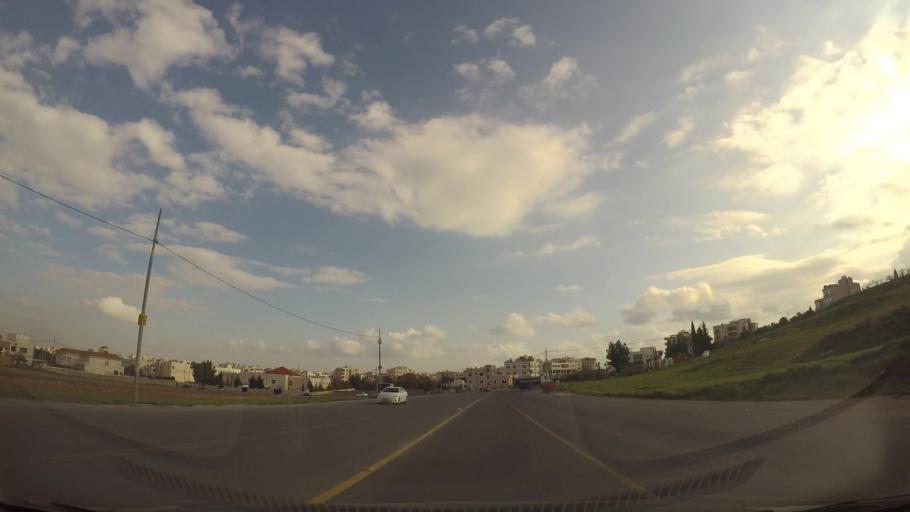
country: JO
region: Amman
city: Umm as Summaq
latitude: 31.9132
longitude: 35.8504
